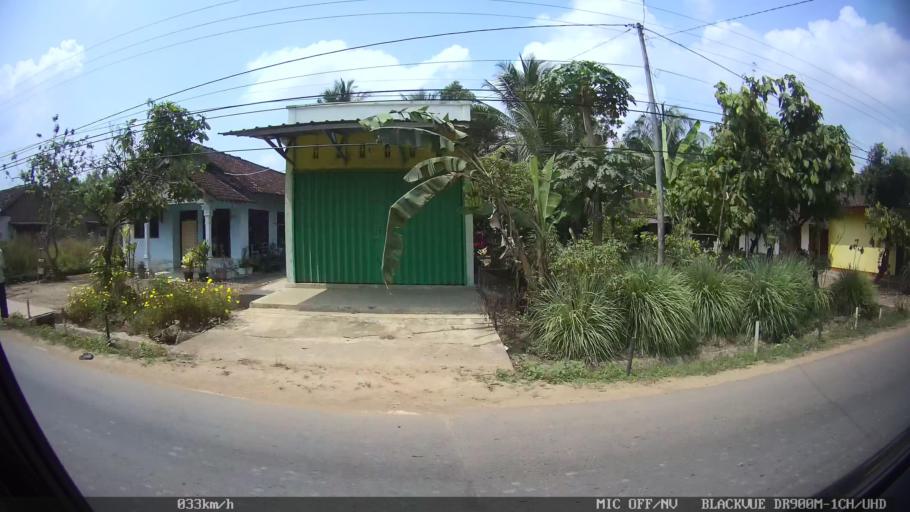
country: ID
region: Lampung
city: Pringsewu
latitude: -5.3872
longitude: 104.9672
